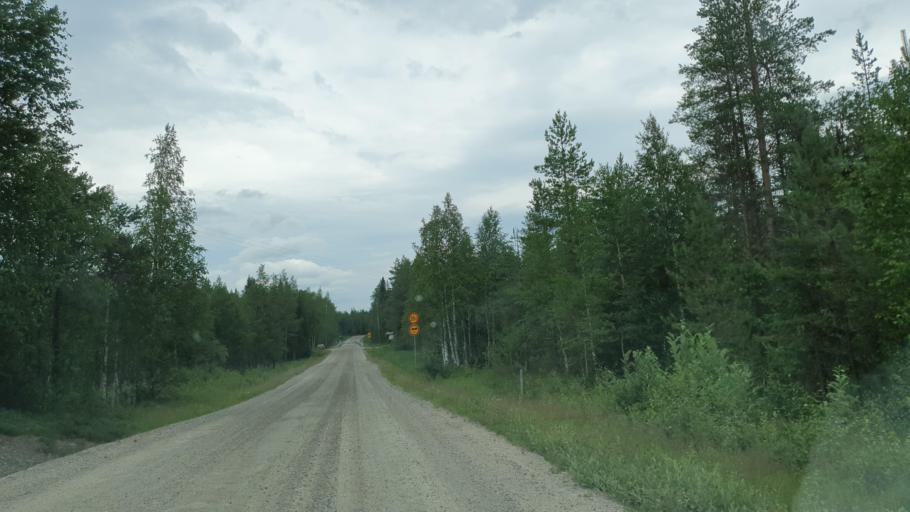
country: RU
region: Republic of Karelia
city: Kostomuksha
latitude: 64.7552
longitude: 29.9230
